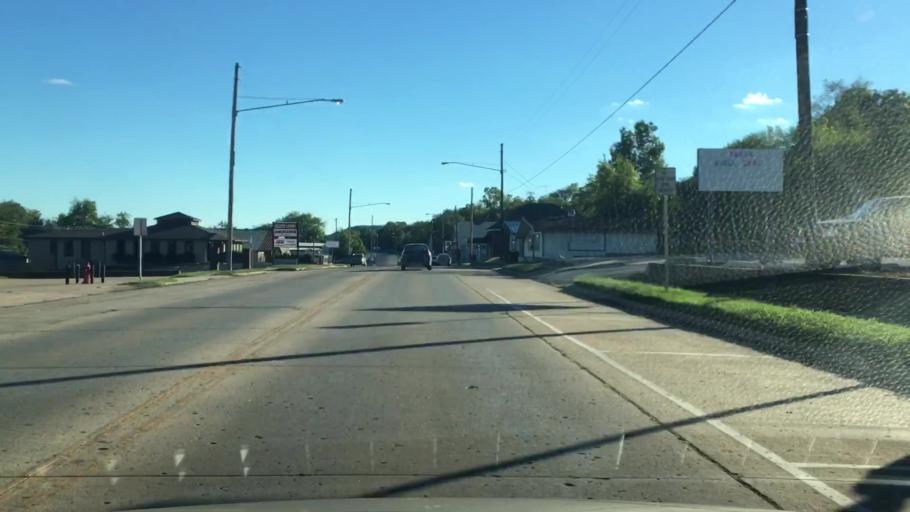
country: US
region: Oklahoma
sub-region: Cherokee County
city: Tahlequah
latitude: 35.9092
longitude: -94.9729
